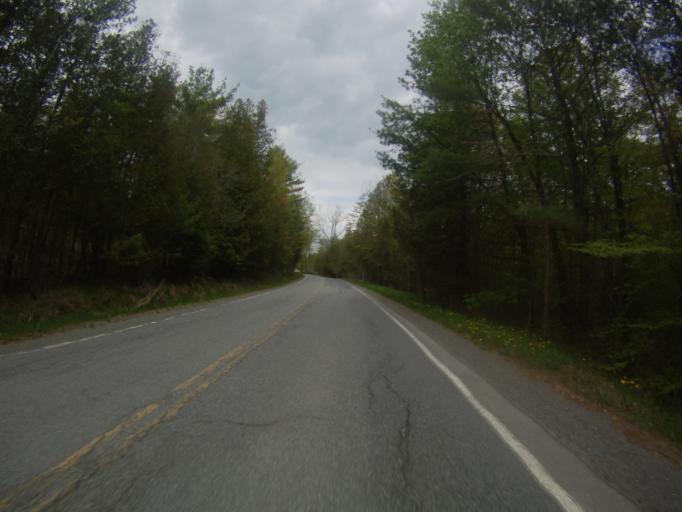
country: US
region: New York
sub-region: Essex County
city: Port Henry
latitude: 43.9374
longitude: -73.5046
